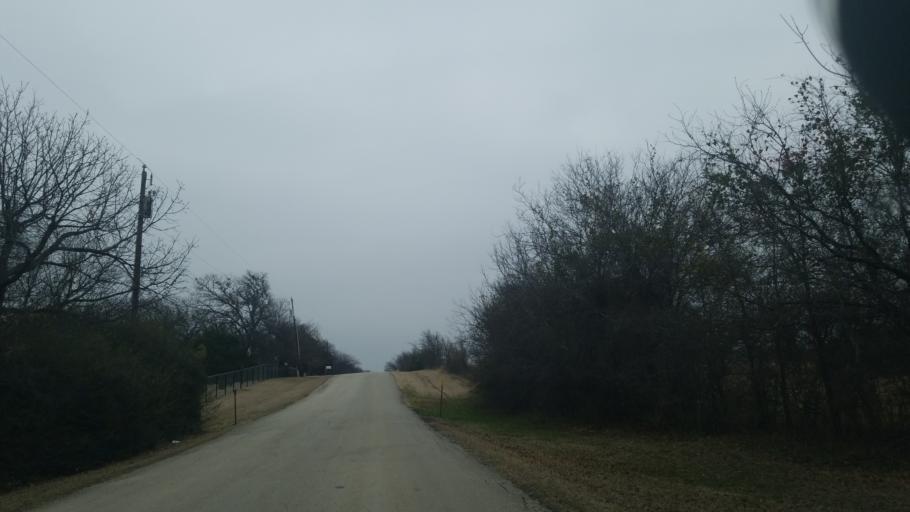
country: US
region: Texas
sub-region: Denton County
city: Argyle
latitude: 33.1472
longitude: -97.1522
